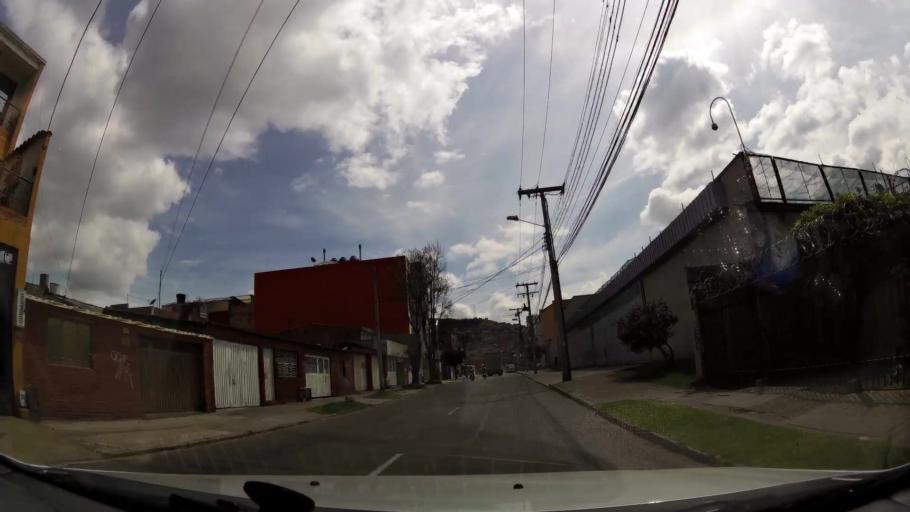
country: CO
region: Bogota D.C.
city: Bogota
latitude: 4.5692
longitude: -74.0988
